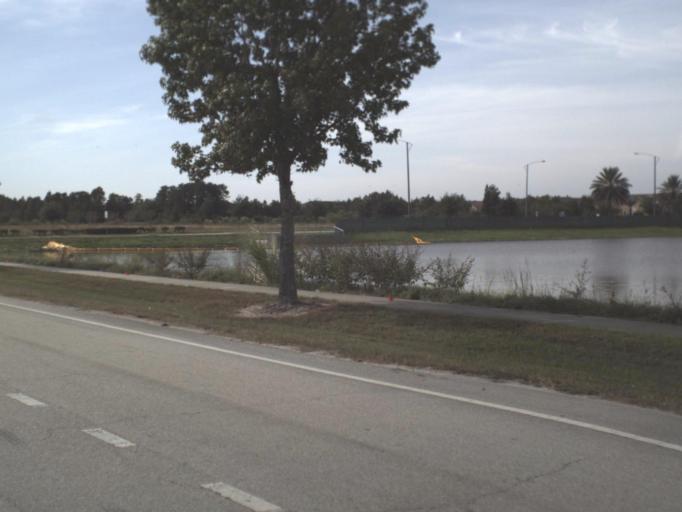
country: US
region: Florida
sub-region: Orange County
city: Oak Ridge
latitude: 28.4954
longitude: -81.4176
